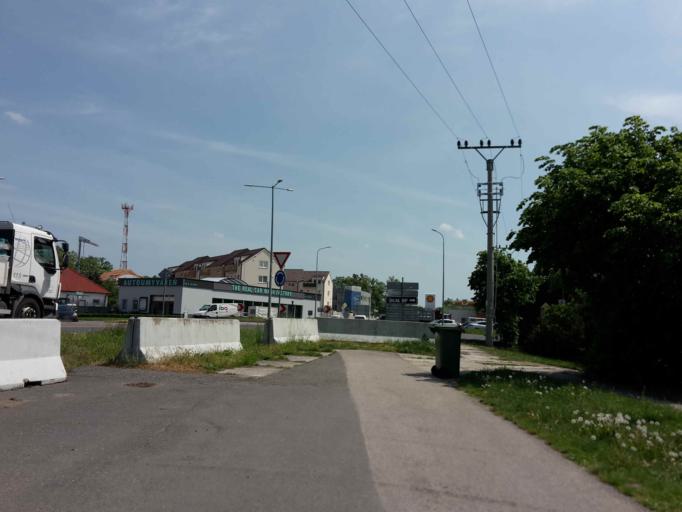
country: SK
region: Bratislavsky
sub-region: Okres Malacky
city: Malacky
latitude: 48.4296
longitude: 17.0347
